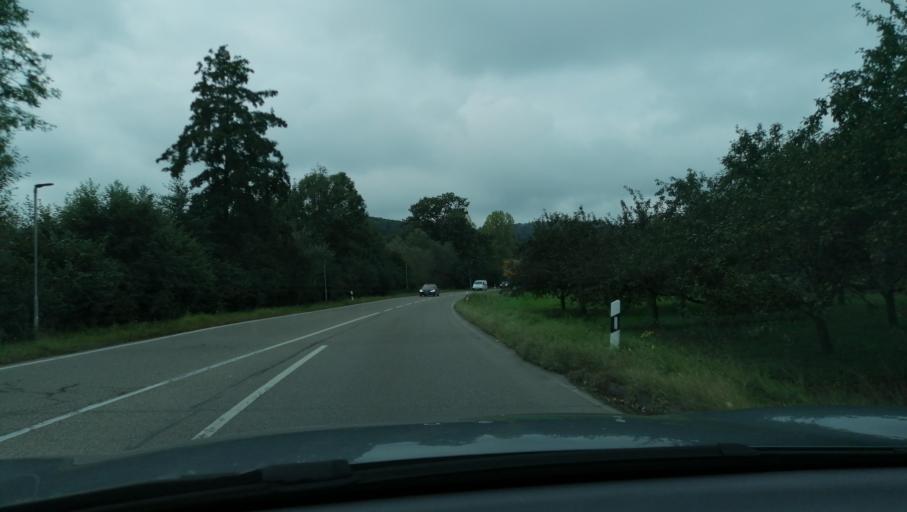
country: DE
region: Baden-Wuerttemberg
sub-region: Regierungsbezirk Stuttgart
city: Winnenden
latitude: 48.8683
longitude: 9.4210
